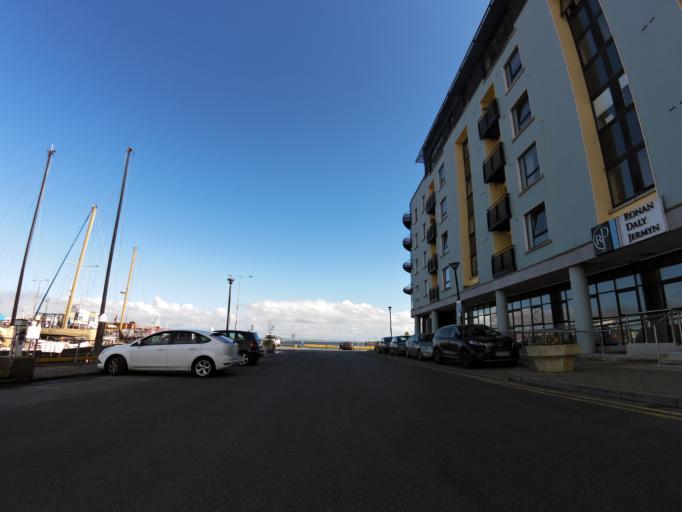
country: IE
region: Connaught
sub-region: County Galway
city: Gaillimh
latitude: 53.2690
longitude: -9.0503
